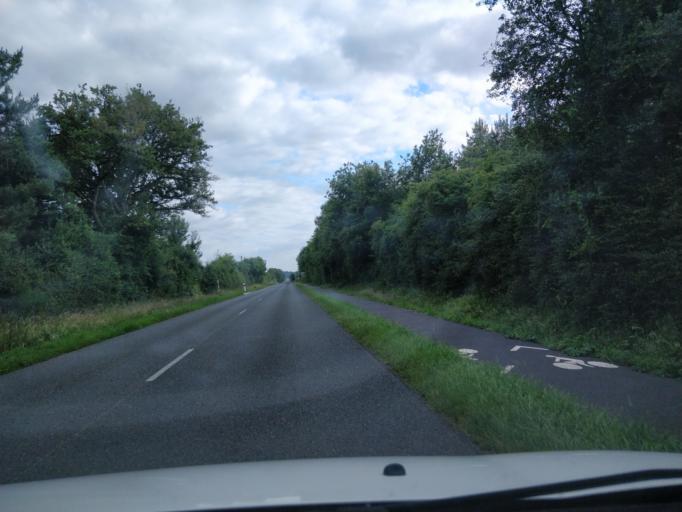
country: FR
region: Pays de la Loire
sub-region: Departement de Maine-et-Loire
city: Feneu
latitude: 47.5621
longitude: -0.5983
